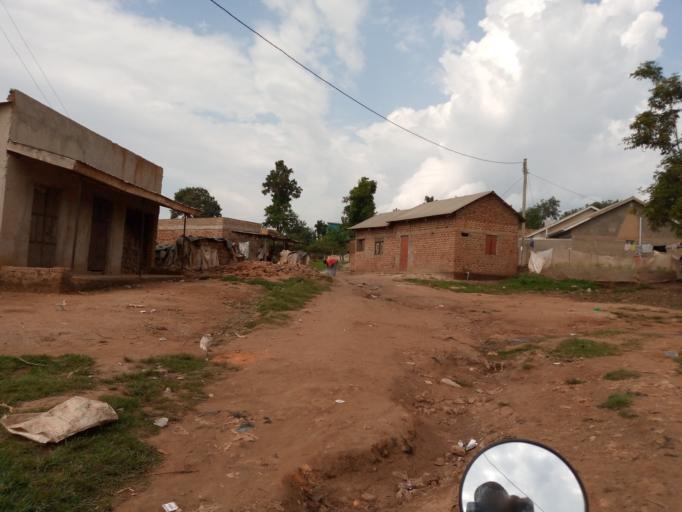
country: UG
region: Eastern Region
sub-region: Mbale District
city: Mbale
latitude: 1.0824
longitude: 34.1655
